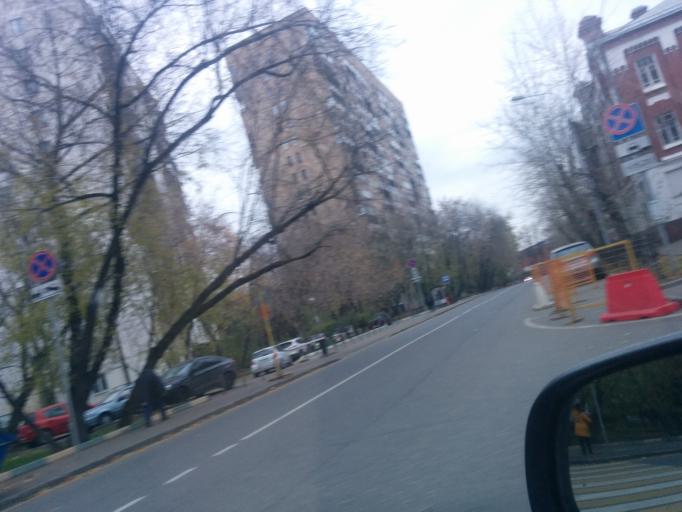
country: RU
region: Moskovskaya
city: Dorogomilovo
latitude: 55.7706
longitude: 37.5729
